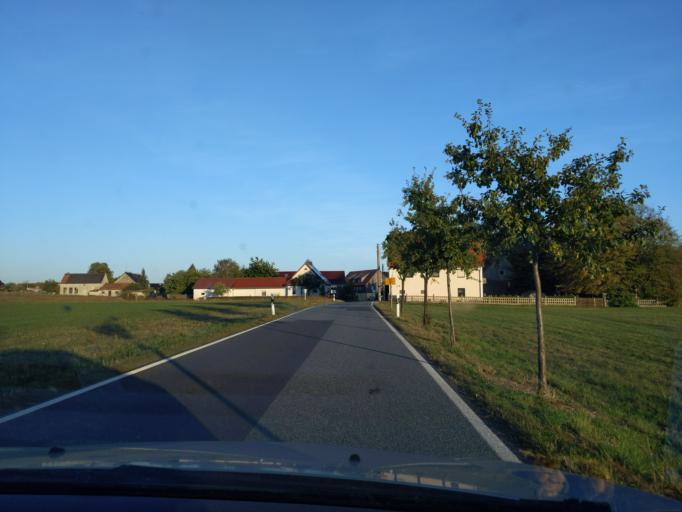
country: DE
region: Saxony
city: Guttau
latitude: 51.2744
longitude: 14.5772
